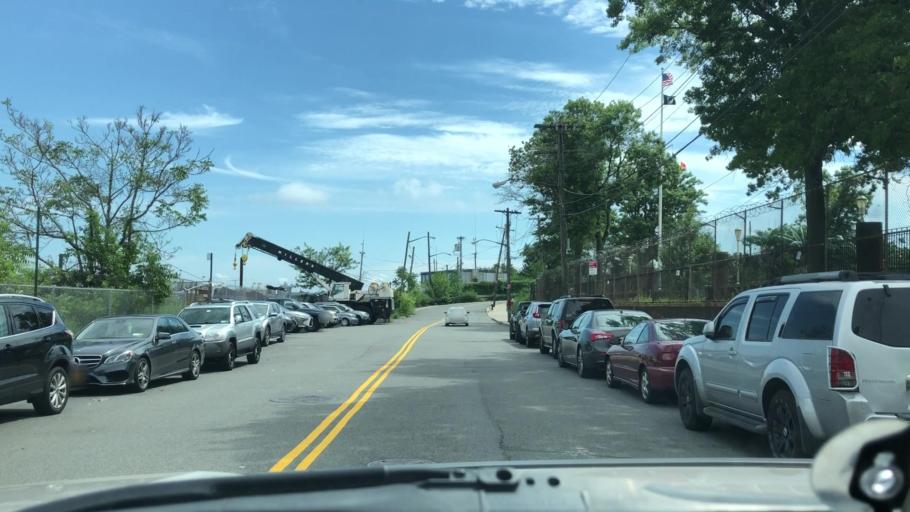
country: US
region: New Jersey
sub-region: Hudson County
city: Bayonne
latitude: 40.6376
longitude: -74.0737
